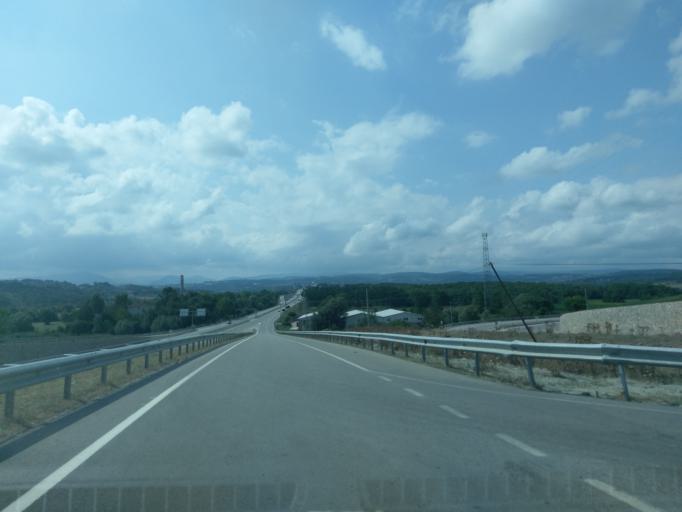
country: TR
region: Sinop
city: Kabali
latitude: 41.9280
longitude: 35.0834
